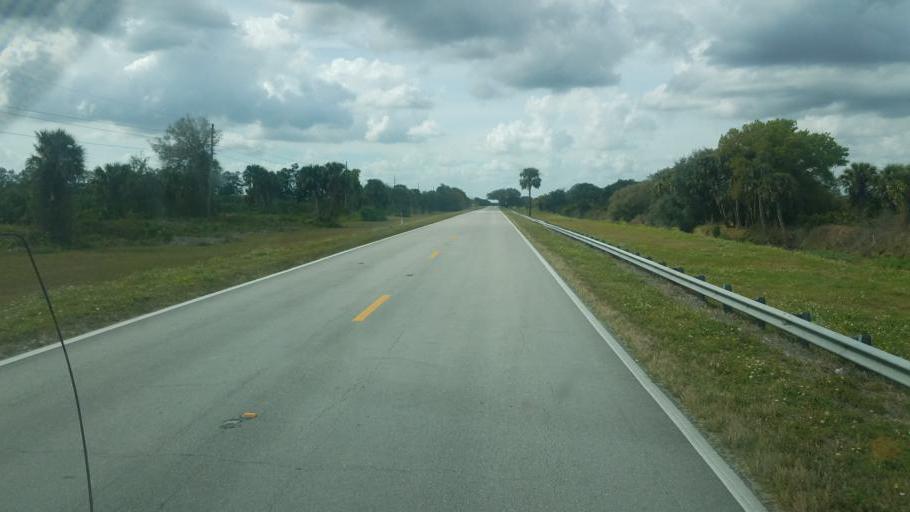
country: US
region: Florida
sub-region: Okeechobee County
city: Cypress Quarters
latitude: 27.4485
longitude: -80.6550
